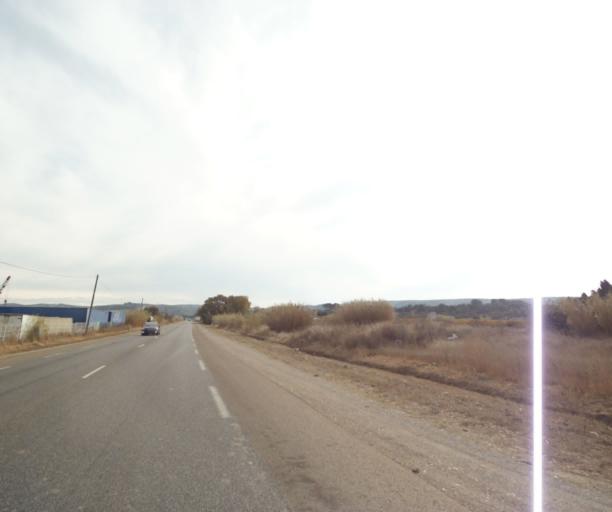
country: FR
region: Provence-Alpes-Cote d'Azur
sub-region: Departement des Bouches-du-Rhone
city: Marignane
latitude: 43.3919
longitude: 5.2070
